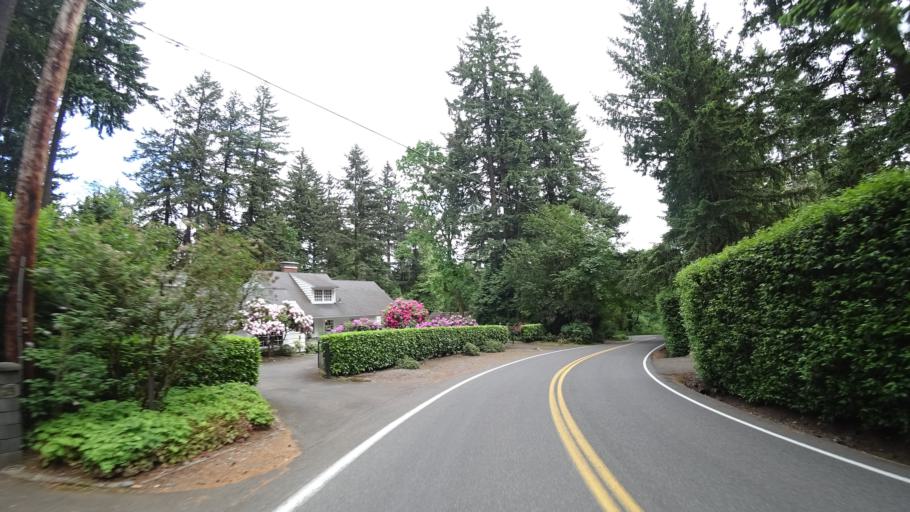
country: US
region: Oregon
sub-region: Clackamas County
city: Lake Oswego
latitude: 45.4447
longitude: -122.6645
